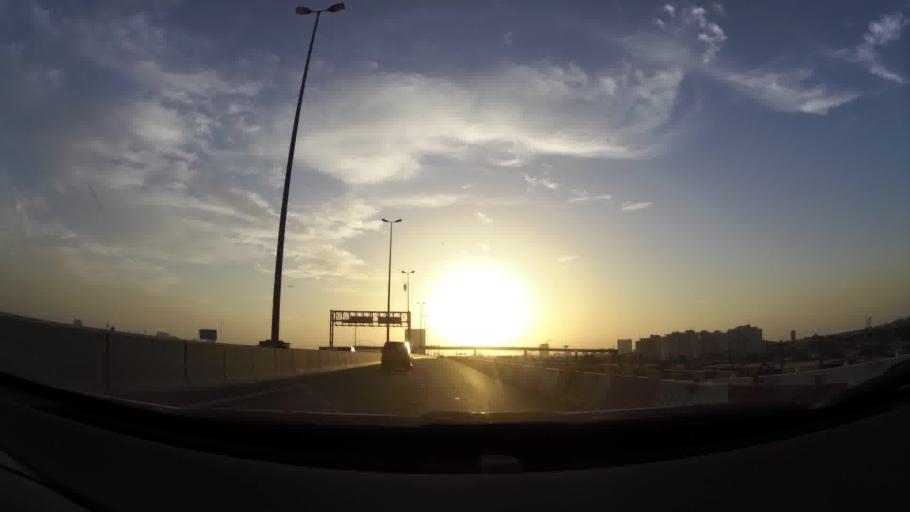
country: KW
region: Al Asimah
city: Ash Shamiyah
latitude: 29.3416
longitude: 47.9282
